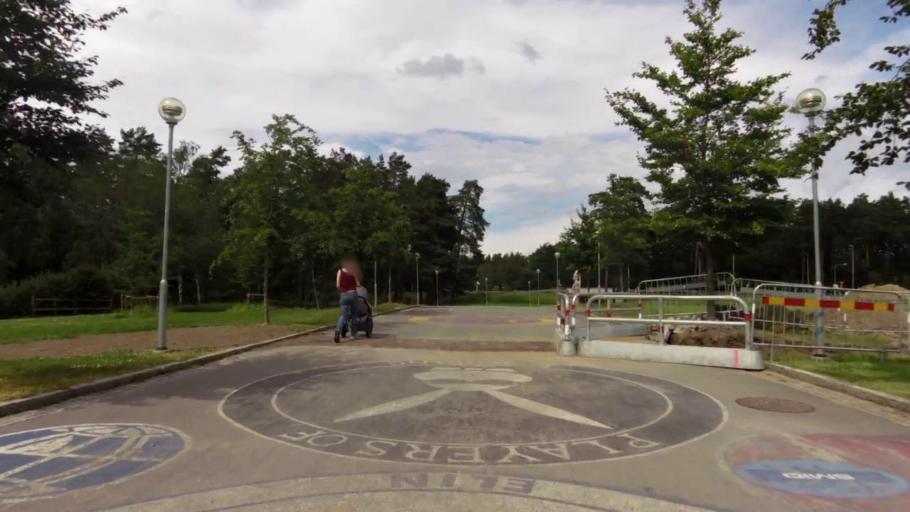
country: SE
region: OEstergoetland
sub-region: Linkopings Kommun
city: Linkoping
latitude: 58.4038
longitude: 15.5776
